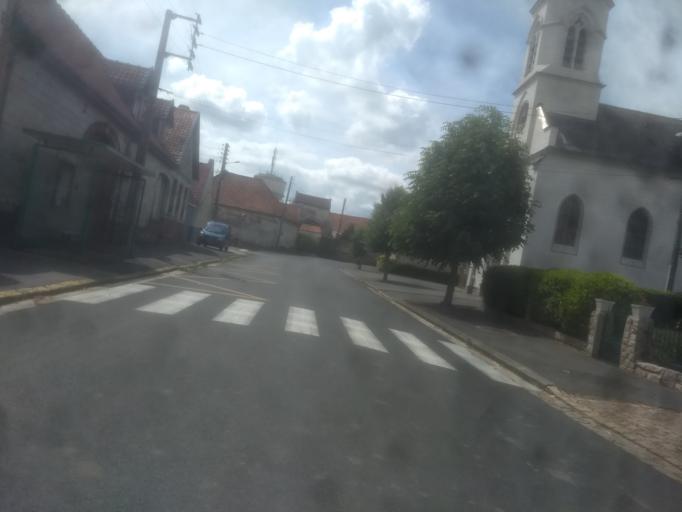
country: FR
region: Nord-Pas-de-Calais
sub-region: Departement du Pas-de-Calais
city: Duisans
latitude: 50.3288
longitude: 2.6388
